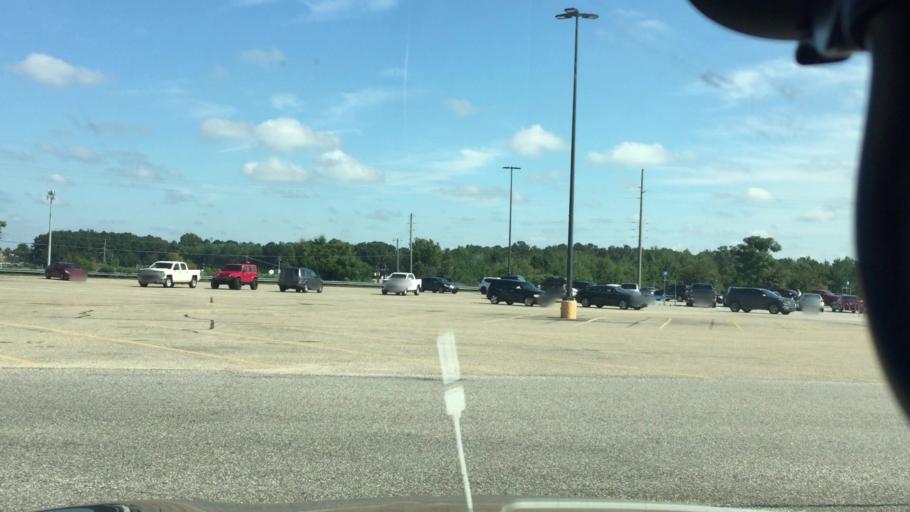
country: US
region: Alabama
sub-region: Coffee County
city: Enterprise
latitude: 31.3157
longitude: -85.8286
